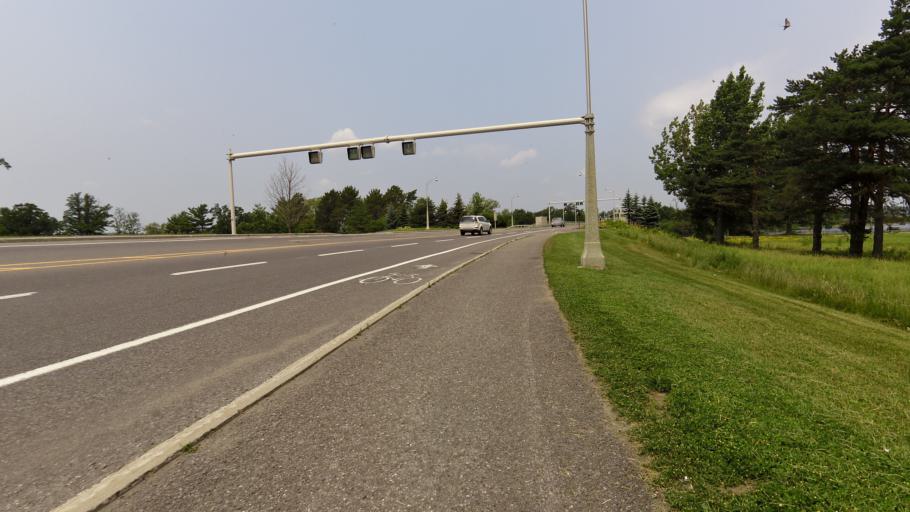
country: CA
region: Ontario
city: Ottawa
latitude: 45.4036
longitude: -75.7545
